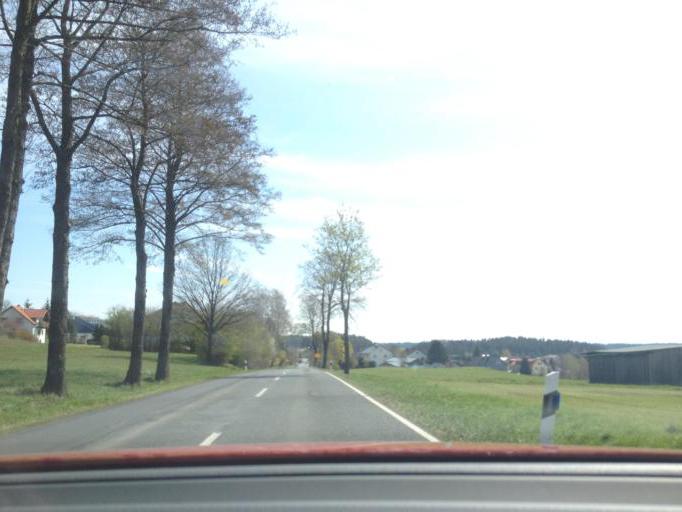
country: DE
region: Bavaria
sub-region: Upper Franconia
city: Hochstadt bei Thiersheim
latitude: 50.0725
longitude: 12.0477
